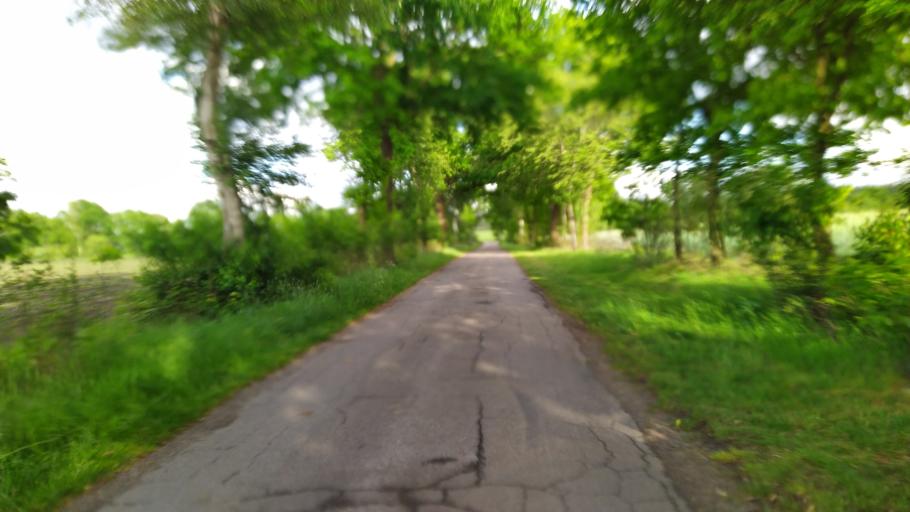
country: DE
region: Lower Saxony
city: Kutenholz
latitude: 53.4637
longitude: 9.3161
